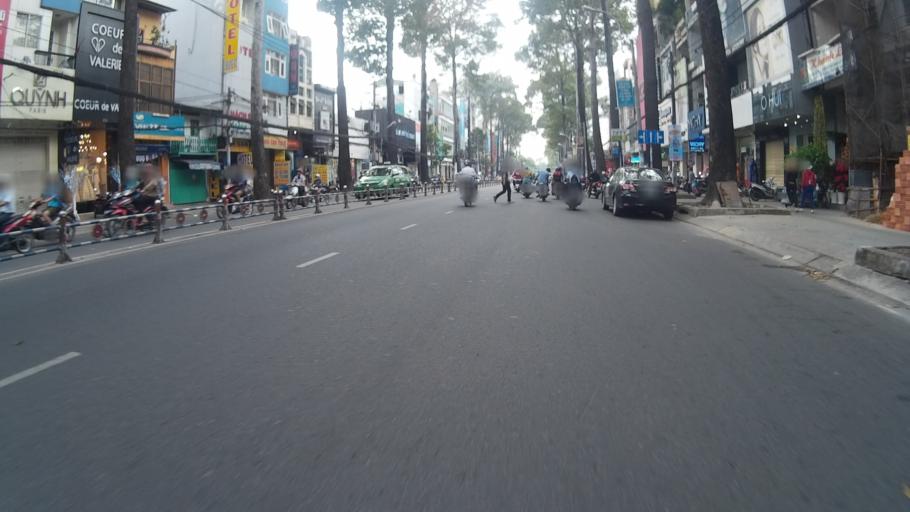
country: VN
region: Ho Chi Minh City
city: Quan Ba
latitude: 10.7753
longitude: 106.6796
